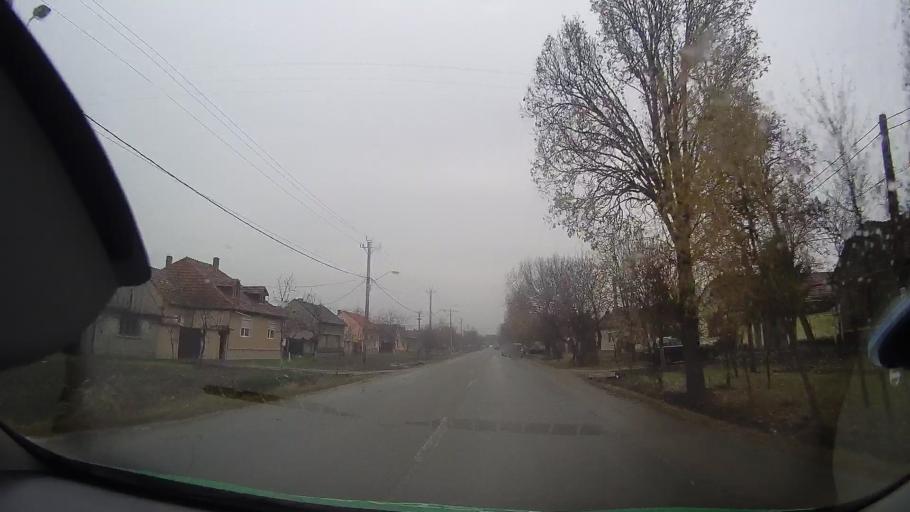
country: RO
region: Bihor
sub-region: Municipiul Salonta
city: Salonta
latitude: 46.7993
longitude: 21.6510
